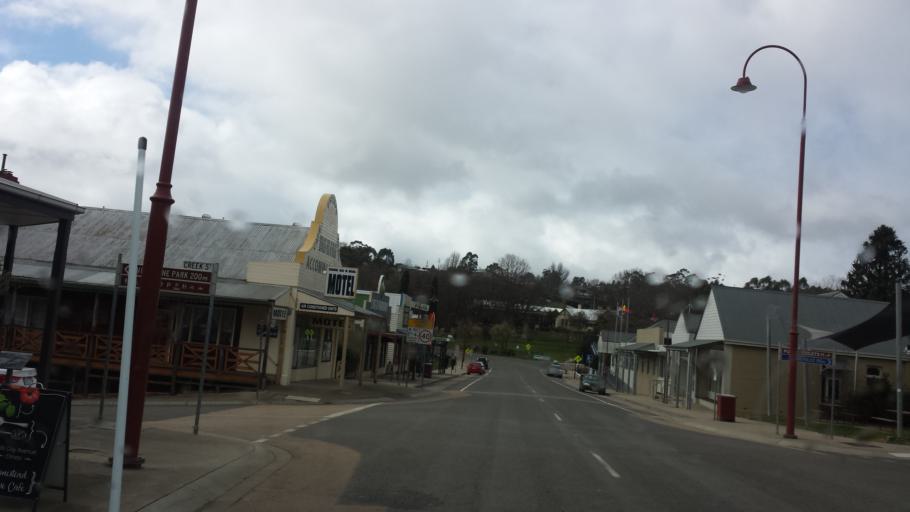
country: AU
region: Victoria
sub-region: Alpine
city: Mount Beauty
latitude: -37.1007
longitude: 147.5909
